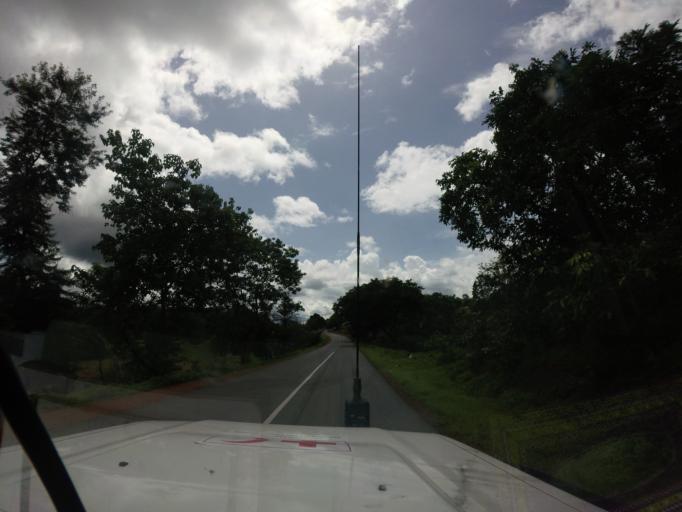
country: SL
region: Northern Province
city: Bindi
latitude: 10.1567
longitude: -11.4900
